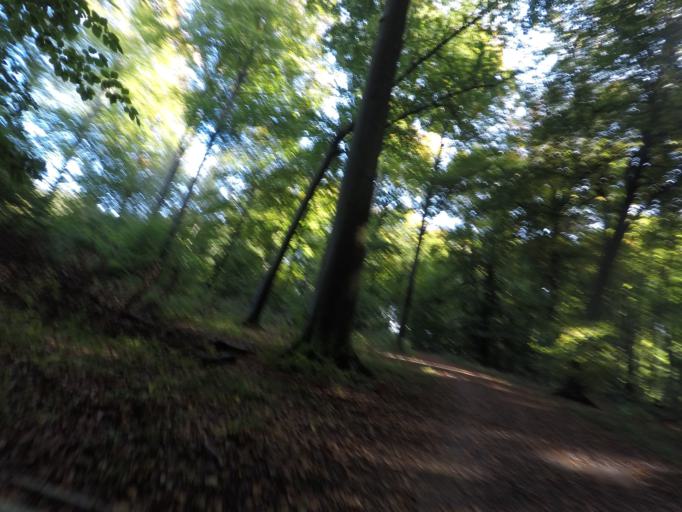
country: LU
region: Luxembourg
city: Itzig
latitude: 49.5971
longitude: 6.1649
